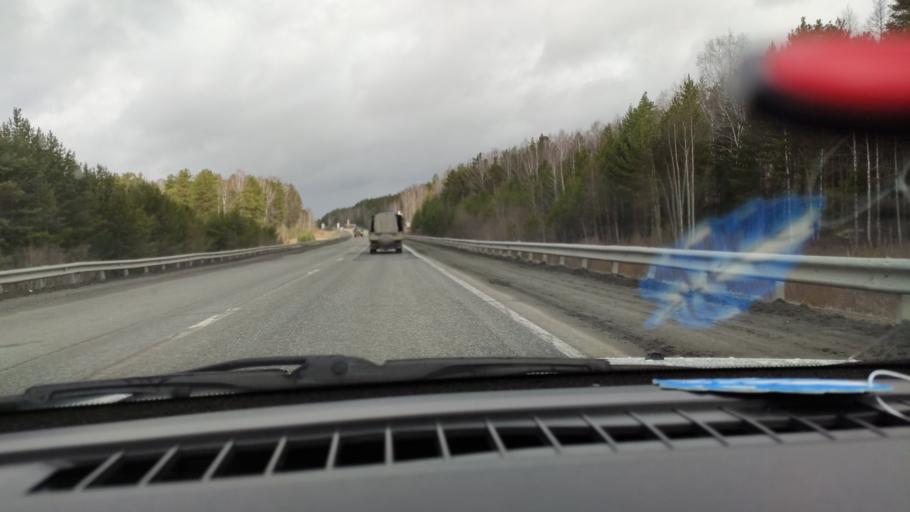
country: RU
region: Sverdlovsk
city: Talitsa
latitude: 56.8682
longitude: 60.0438
